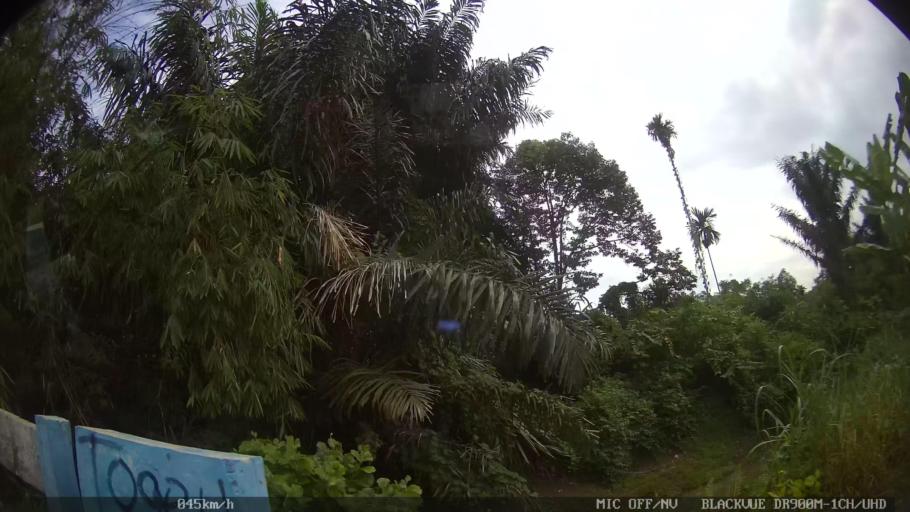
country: ID
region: North Sumatra
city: Sunggal
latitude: 3.5727
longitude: 98.5804
